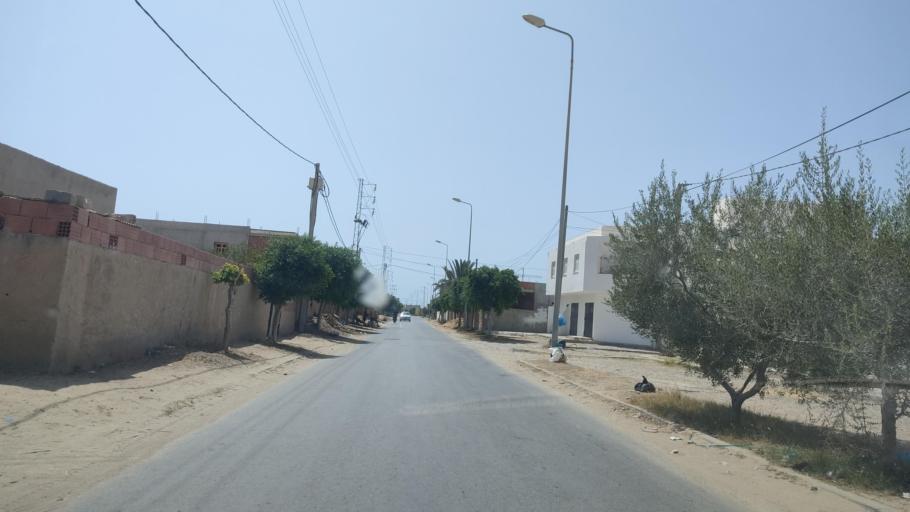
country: TN
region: Safaqis
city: Sfax
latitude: 34.6717
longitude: 10.7040
